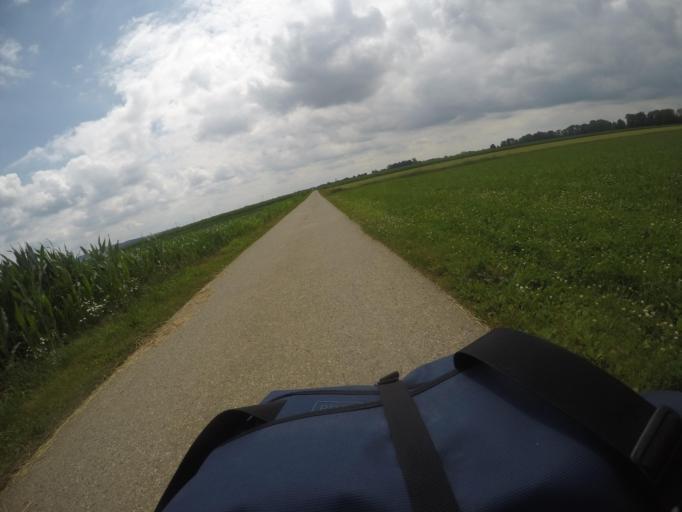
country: DE
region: Bavaria
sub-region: Swabia
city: Fellheim
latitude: 48.0618
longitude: 10.1561
